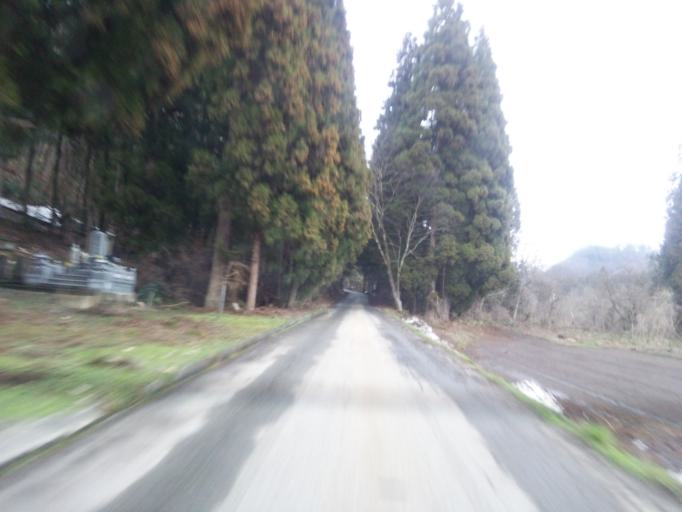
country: JP
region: Fukushima
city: Kitakata
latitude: 37.6747
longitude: 139.9192
